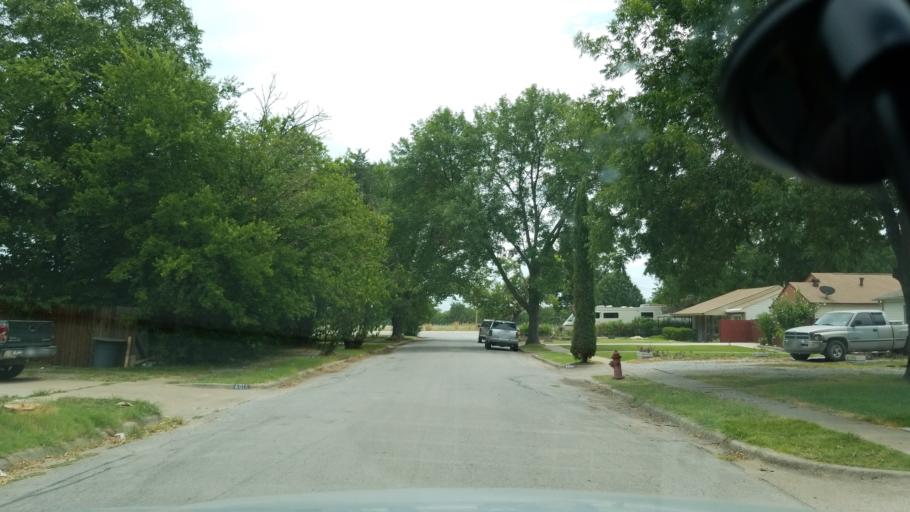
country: US
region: Texas
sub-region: Dallas County
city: Grand Prairie
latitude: 32.7401
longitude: -96.9886
